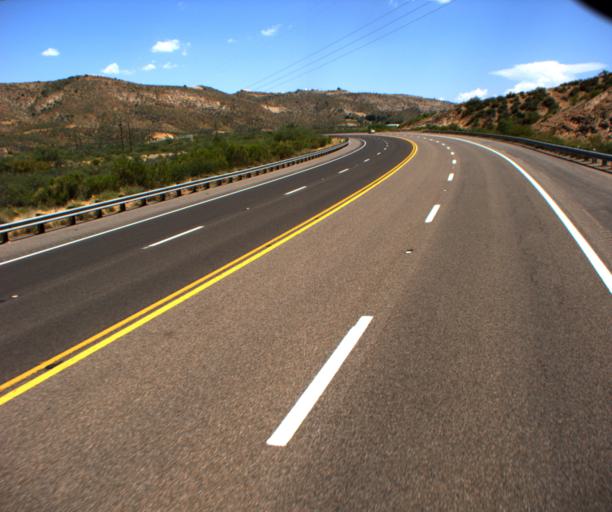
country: US
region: Arizona
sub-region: Gila County
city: Claypool
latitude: 33.4438
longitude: -110.8375
